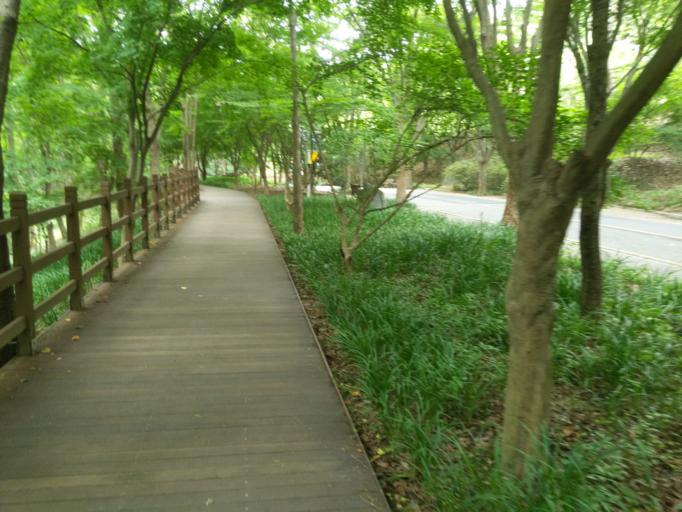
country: KR
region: Daegu
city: Hwawon
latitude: 35.8017
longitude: 128.5214
